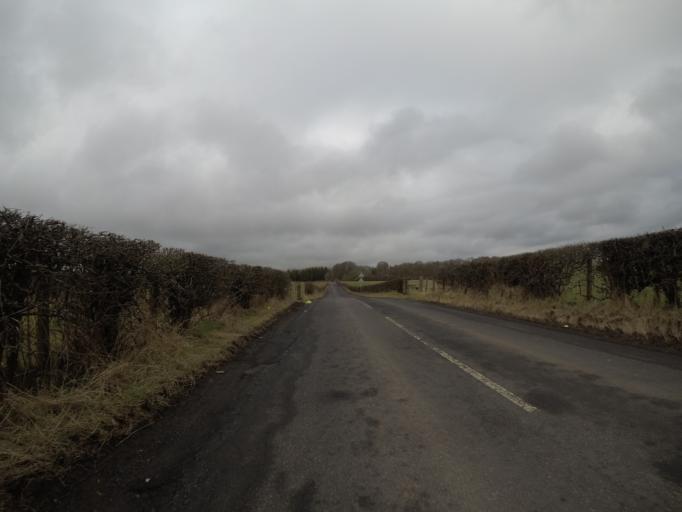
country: GB
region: Scotland
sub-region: North Ayrshire
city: Springside
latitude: 55.6250
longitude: -4.6124
